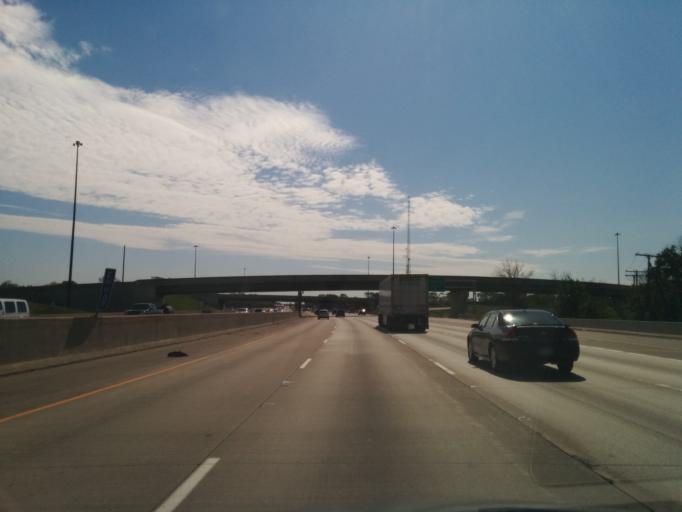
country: US
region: Indiana
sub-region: Lake County
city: Munster
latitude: 41.5741
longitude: -87.5127
